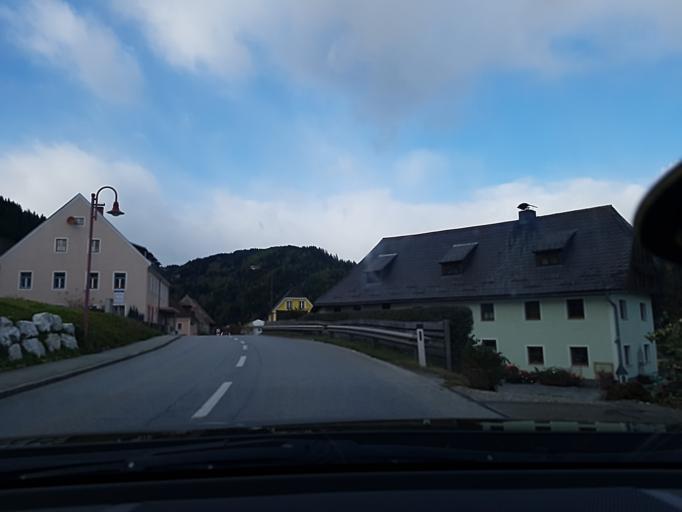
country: AT
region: Styria
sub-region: Politischer Bezirk Murtal
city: Oberzeiring
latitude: 47.2786
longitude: 14.4813
